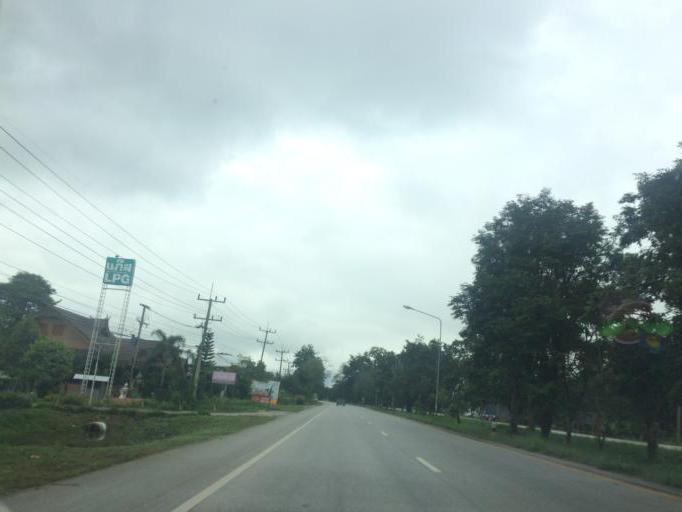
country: TH
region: Chiang Rai
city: Mae Lao
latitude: 19.7593
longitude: 99.7339
